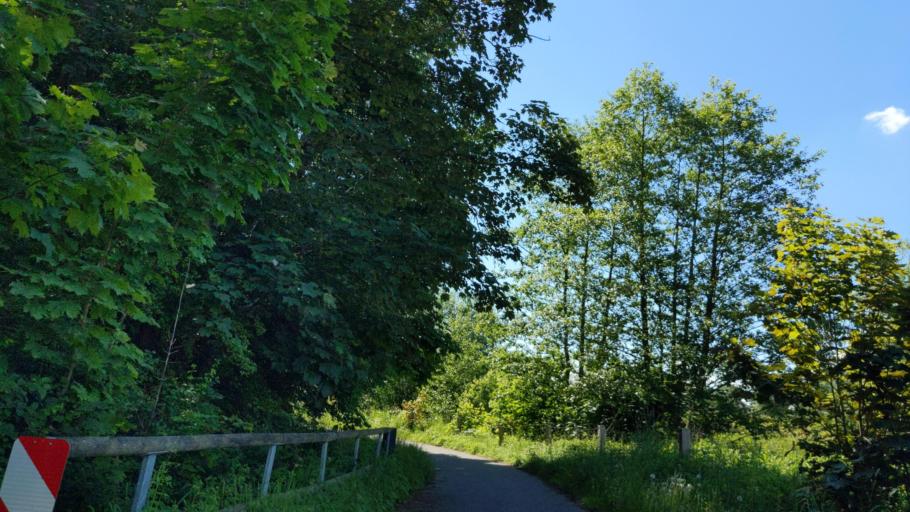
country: DE
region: Schleswig-Holstein
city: Eutin
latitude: 54.1358
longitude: 10.6383
